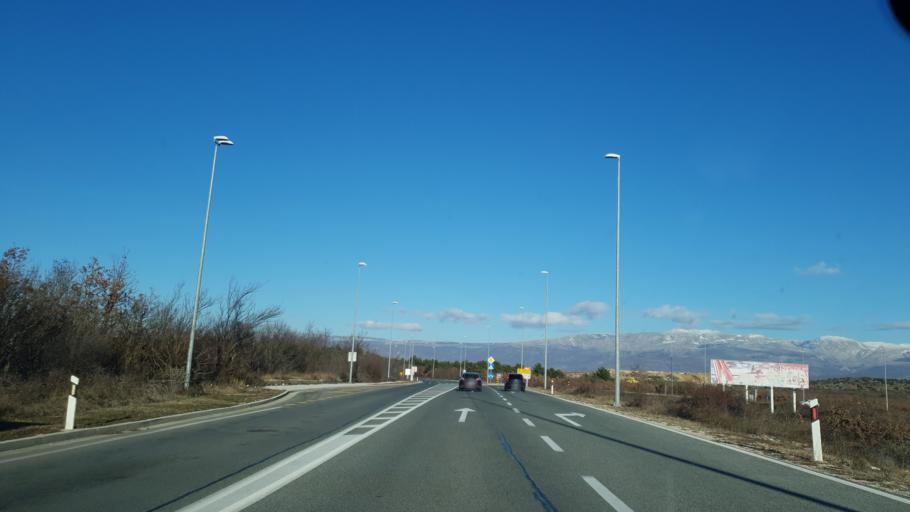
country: HR
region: Splitsko-Dalmatinska
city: Brnaze
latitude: 43.6528
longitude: 16.6378
